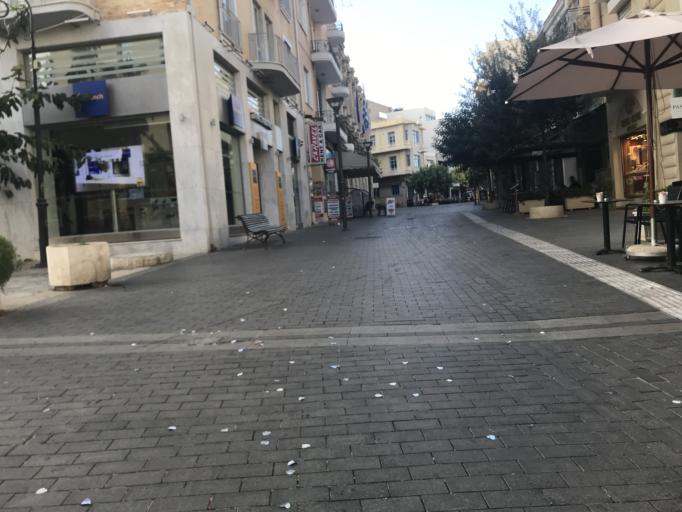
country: GR
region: Crete
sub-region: Nomos Irakleiou
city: Irakleion
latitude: 35.3405
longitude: 25.1338
